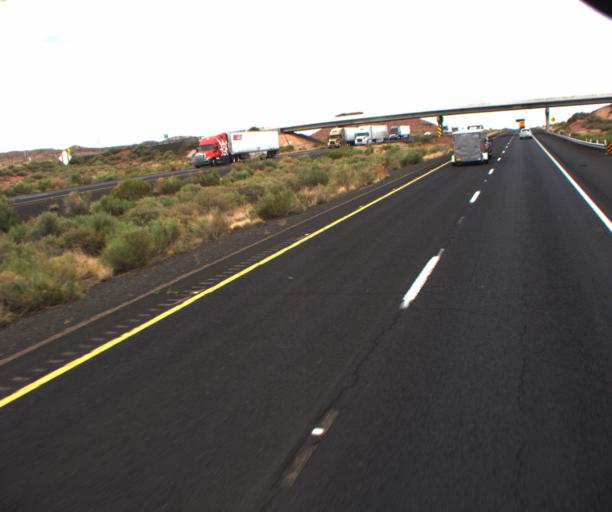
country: US
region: Arizona
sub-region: Navajo County
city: Joseph City
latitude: 34.9235
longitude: -110.2617
